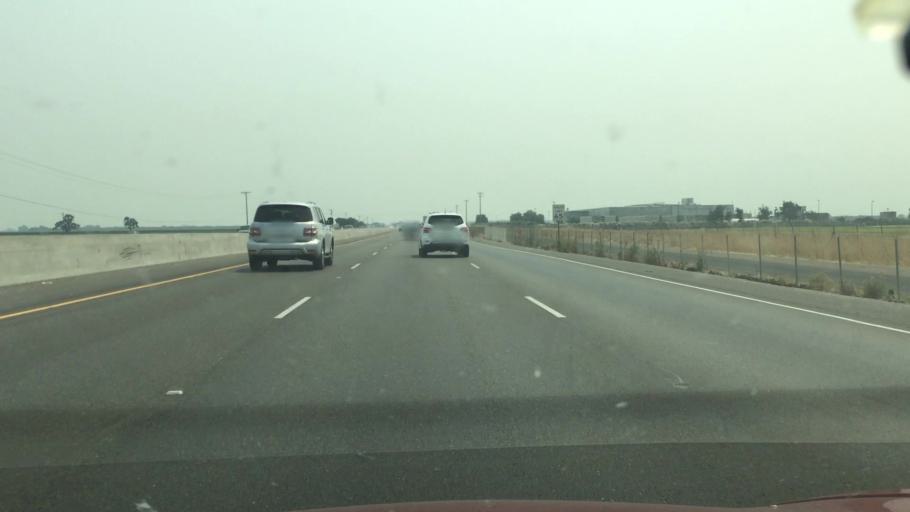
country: US
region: California
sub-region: San Joaquin County
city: Kennedy
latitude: 37.8949
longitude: -121.2205
